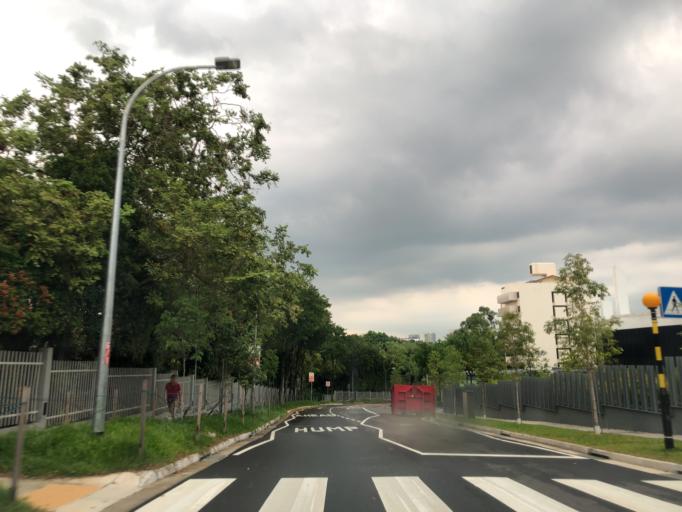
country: SG
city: Singapore
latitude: 1.3009
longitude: 103.8468
